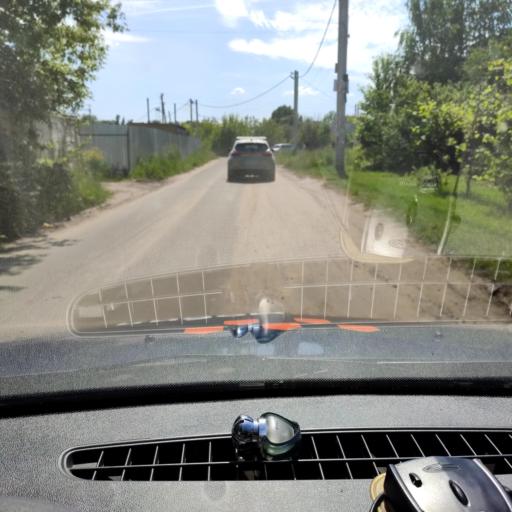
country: RU
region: Voronezj
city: Ramon'
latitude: 51.8283
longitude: 39.2690
